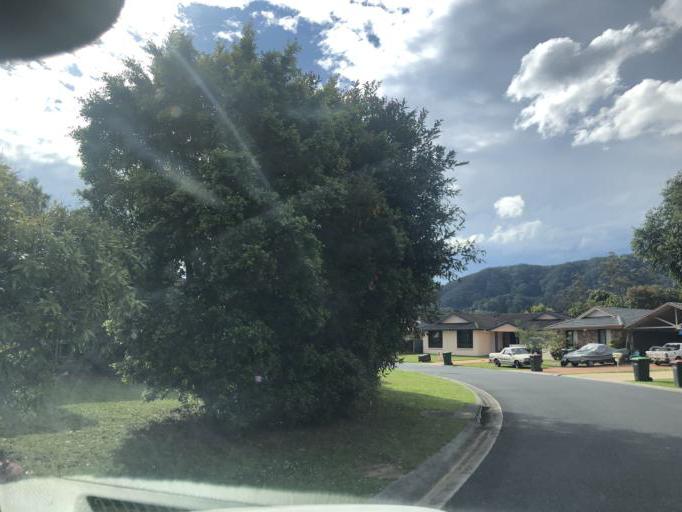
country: AU
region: New South Wales
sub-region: Coffs Harbour
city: Coffs Harbour
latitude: -30.2861
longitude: 153.0996
